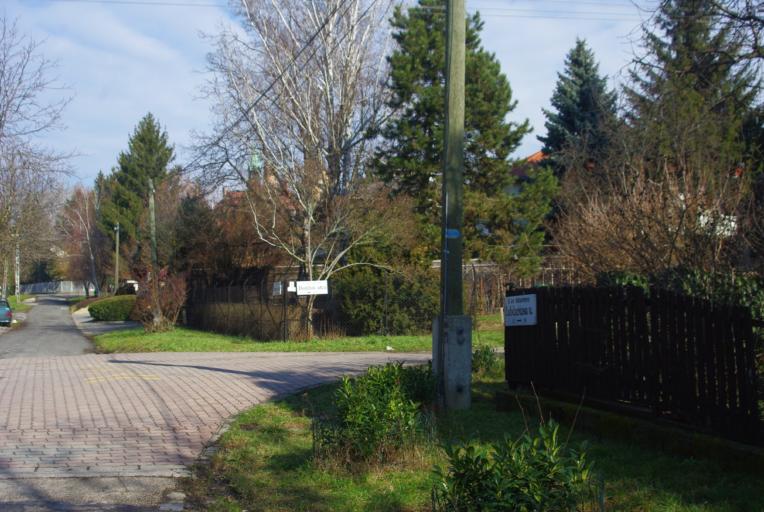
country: HU
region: Pest
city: Solymar
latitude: 47.5587
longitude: 18.9451
